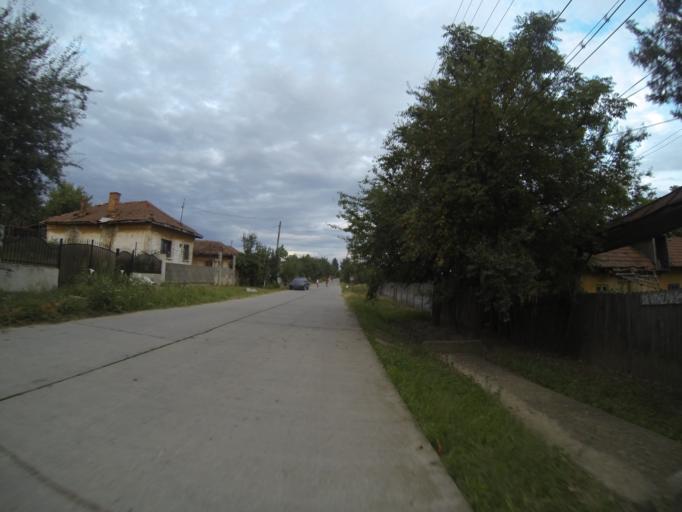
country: RO
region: Dolj
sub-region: Comuna Almaju
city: Almaju
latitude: 44.4282
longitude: 23.7089
